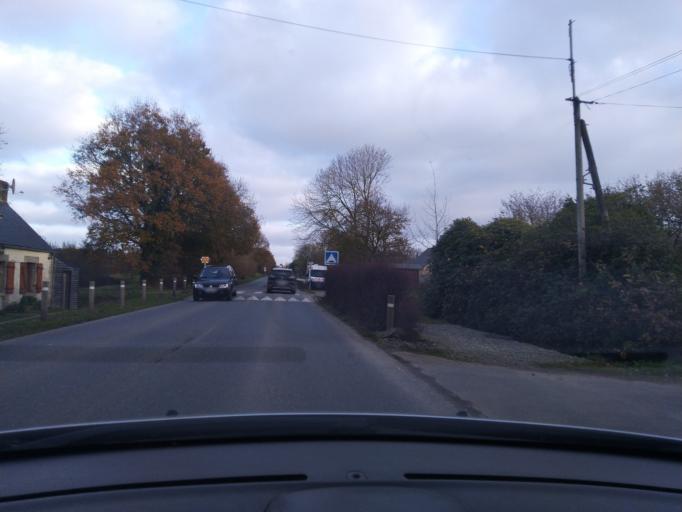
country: FR
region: Brittany
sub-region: Departement du Finistere
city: Plouigneau
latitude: 48.5708
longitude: -3.7158
